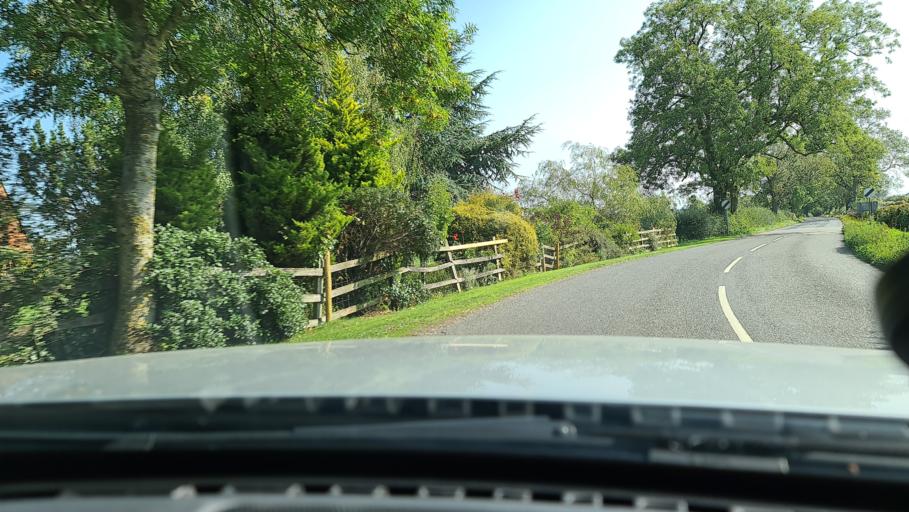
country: GB
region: England
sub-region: Northamptonshire
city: Daventry
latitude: 52.1531
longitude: -1.1541
